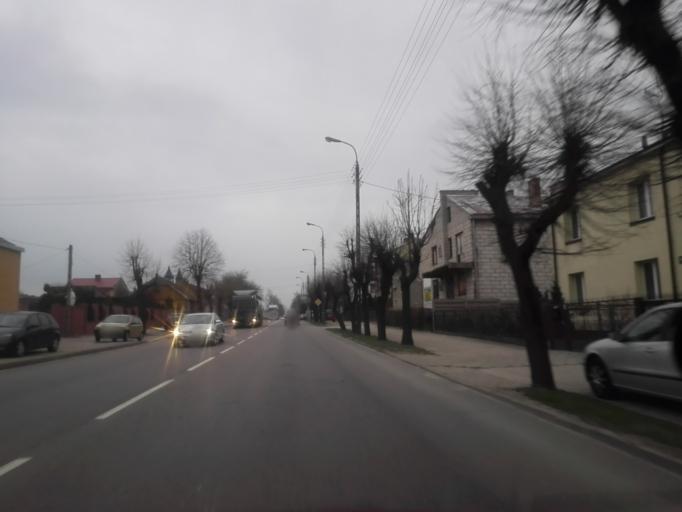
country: PL
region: Podlasie
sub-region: Powiat grajewski
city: Grajewo
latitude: 53.6446
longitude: 22.4493
